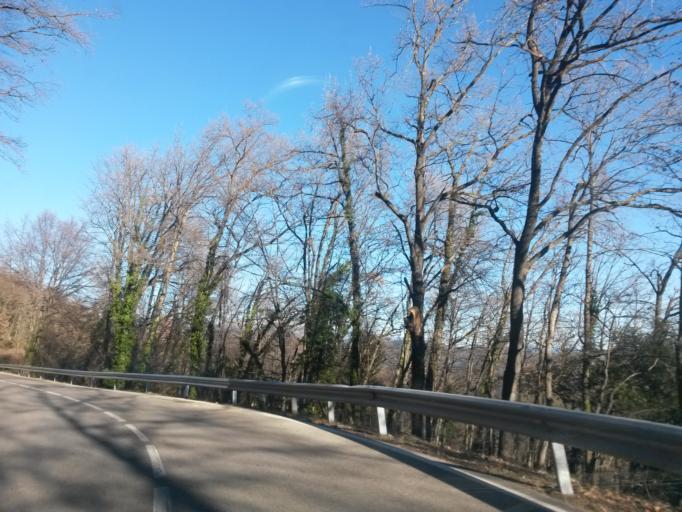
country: ES
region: Catalonia
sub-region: Provincia de Girona
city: Sant Feliu de Pallerols
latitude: 42.0683
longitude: 2.4948
